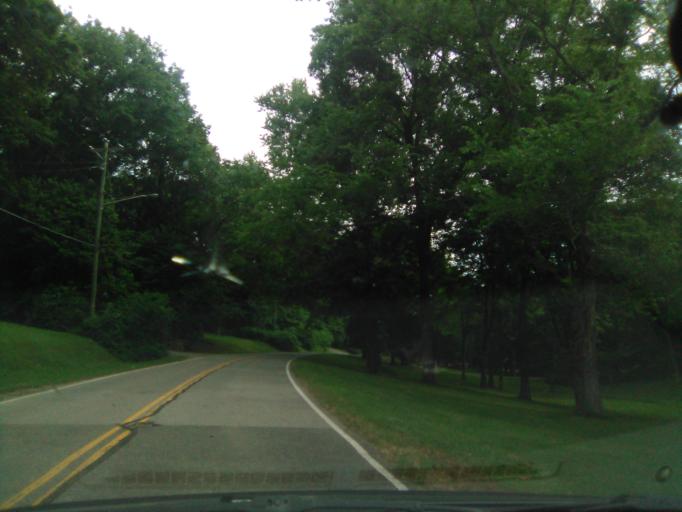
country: US
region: Tennessee
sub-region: Davidson County
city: Belle Meade
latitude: 36.0997
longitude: -86.8953
